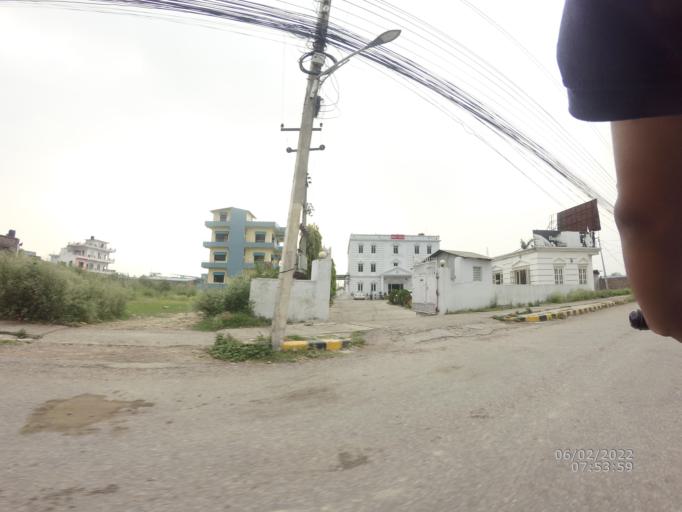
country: NP
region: Western Region
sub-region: Lumbini Zone
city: Bhairahawa
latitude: 27.5033
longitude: 83.4573
